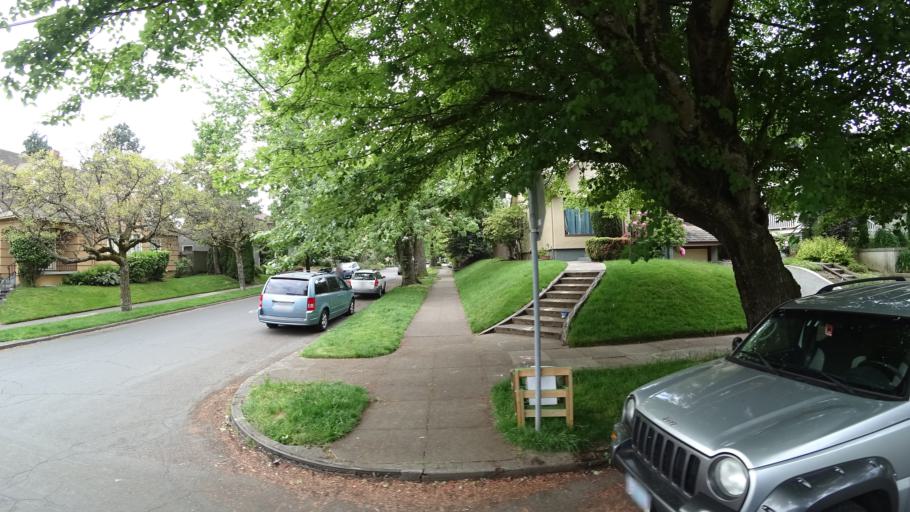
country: US
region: Oregon
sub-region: Multnomah County
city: Portland
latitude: 45.5453
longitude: -122.6535
